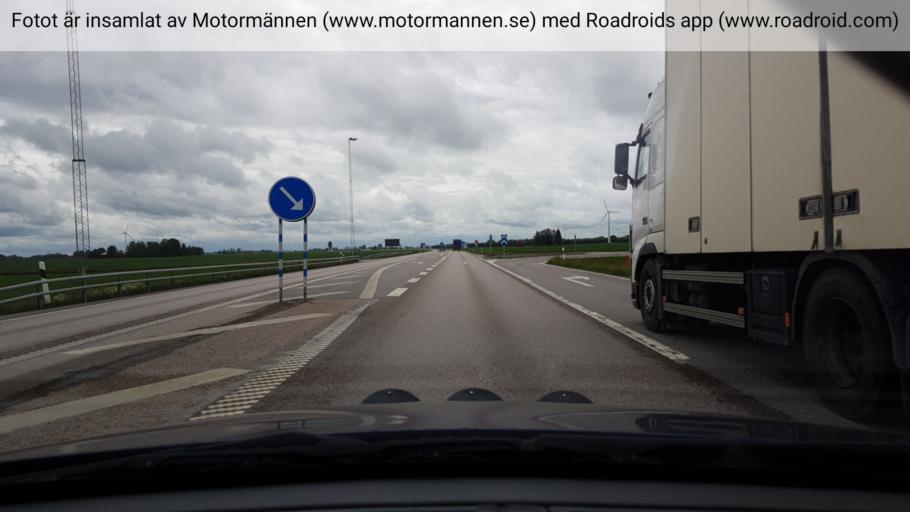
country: SE
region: Vaestra Goetaland
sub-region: Vara Kommun
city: Kvanum
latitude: 58.3398
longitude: 13.1547
